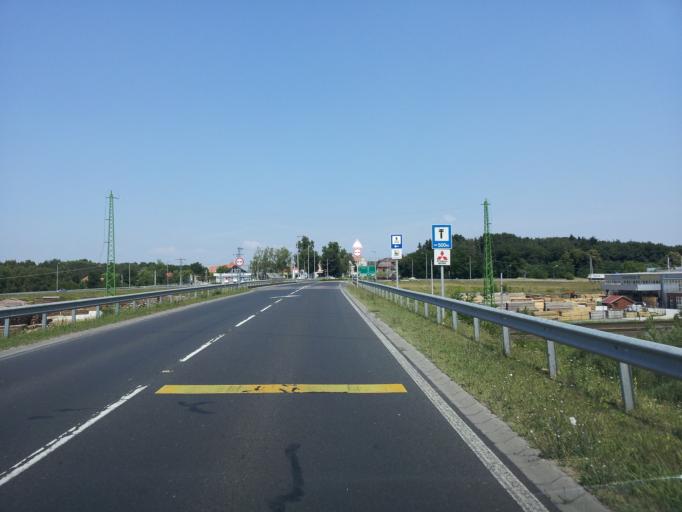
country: HU
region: Zala
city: Zalaegerszeg
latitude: 46.8601
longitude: 16.8555
